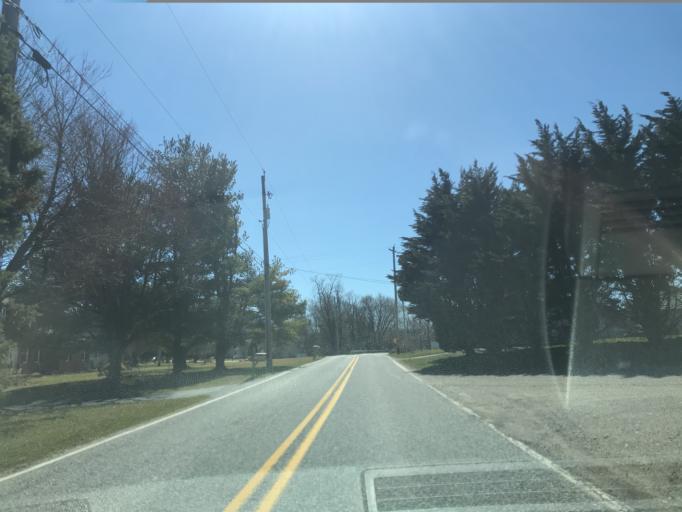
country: US
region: Pennsylvania
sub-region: York County
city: Shrewsbury
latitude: 39.7497
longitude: -76.6597
